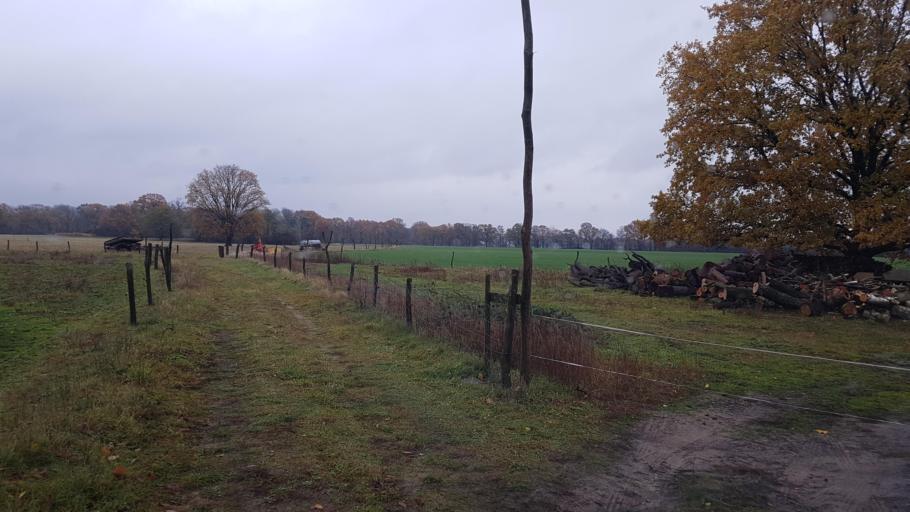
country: DE
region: Brandenburg
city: Drebkau
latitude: 51.6889
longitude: 14.2348
